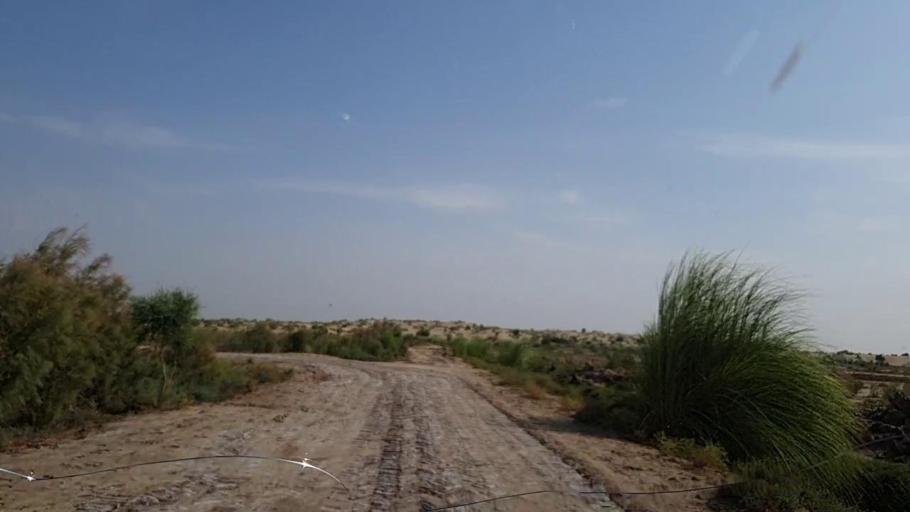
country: PK
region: Sindh
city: Khanpur
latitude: 27.6759
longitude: 69.3685
